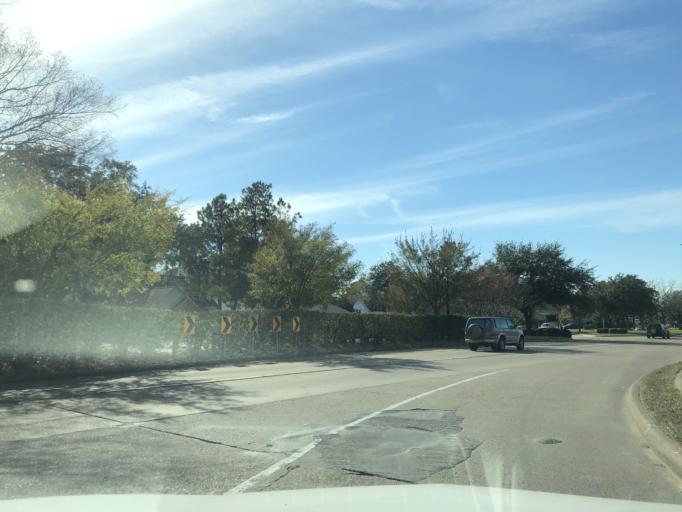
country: US
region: Texas
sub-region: Harris County
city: Bellaire
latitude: 29.6776
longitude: -95.4991
